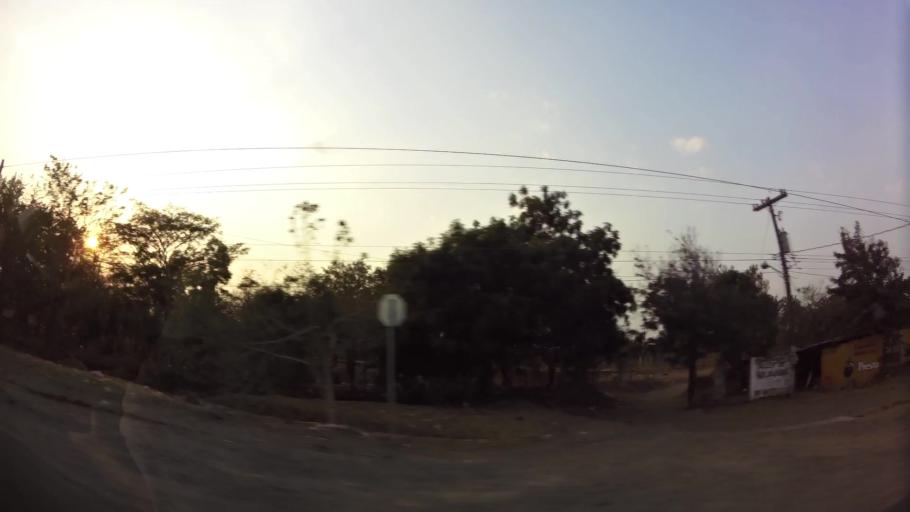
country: NI
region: Leon
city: La Paz Centro
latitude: 12.3344
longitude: -86.6800
